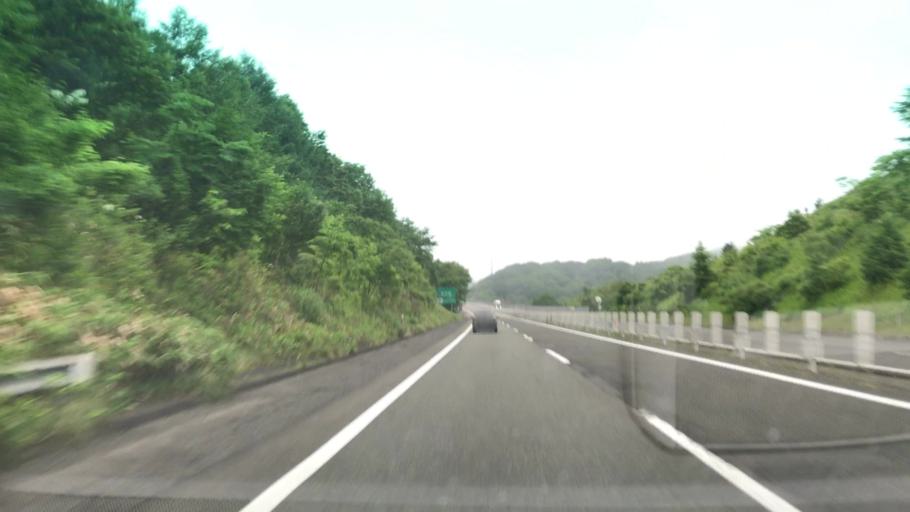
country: JP
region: Hokkaido
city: Shiraoi
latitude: 42.4677
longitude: 141.1923
